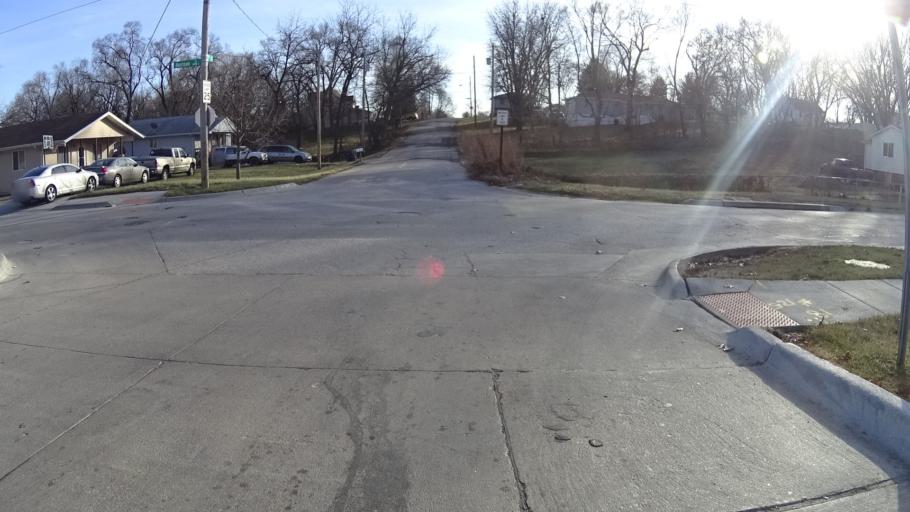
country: US
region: Nebraska
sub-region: Douglas County
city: Omaha
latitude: 41.1911
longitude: -95.9529
